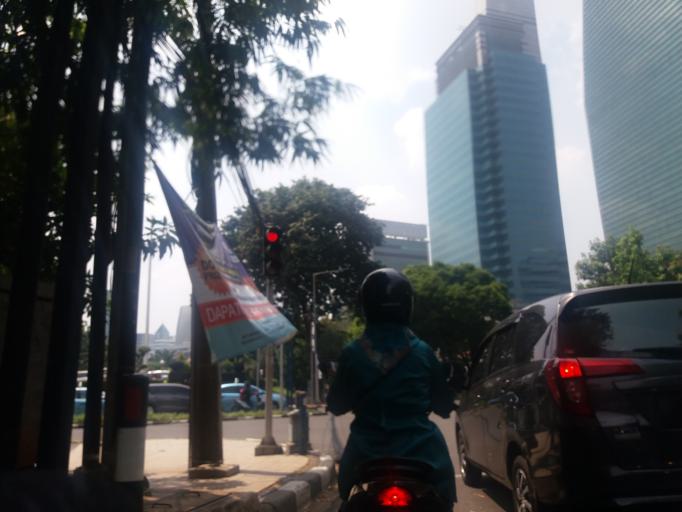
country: ID
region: Jakarta Raya
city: Jakarta
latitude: -6.2329
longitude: 106.8300
